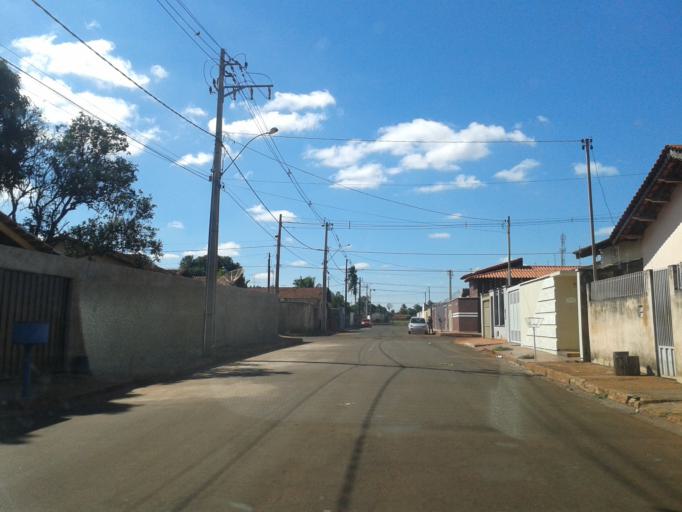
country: BR
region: Minas Gerais
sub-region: Centralina
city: Centralina
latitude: -18.5913
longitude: -49.1983
